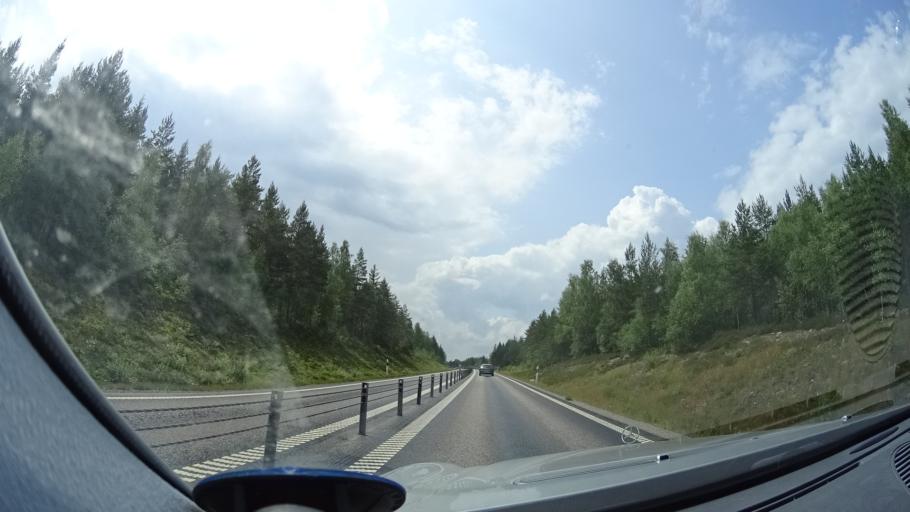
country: SE
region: Kalmar
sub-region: Nybro Kommun
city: Nybro
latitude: 56.7215
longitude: 15.7953
